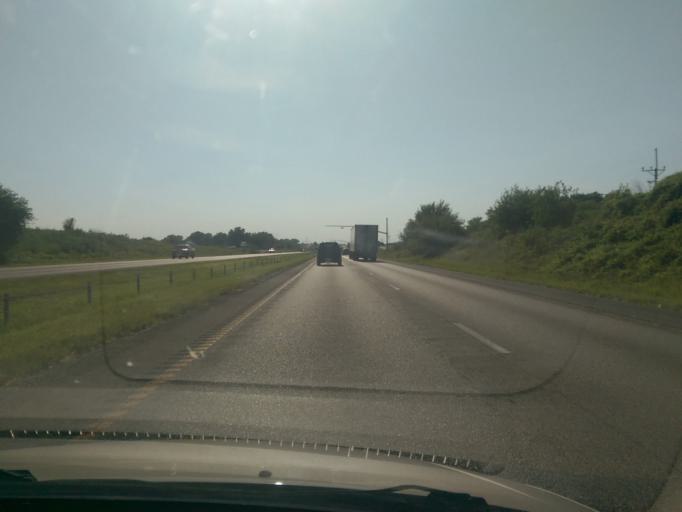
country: US
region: Missouri
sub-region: Lafayette County
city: Higginsville
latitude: 39.0033
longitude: -93.8248
